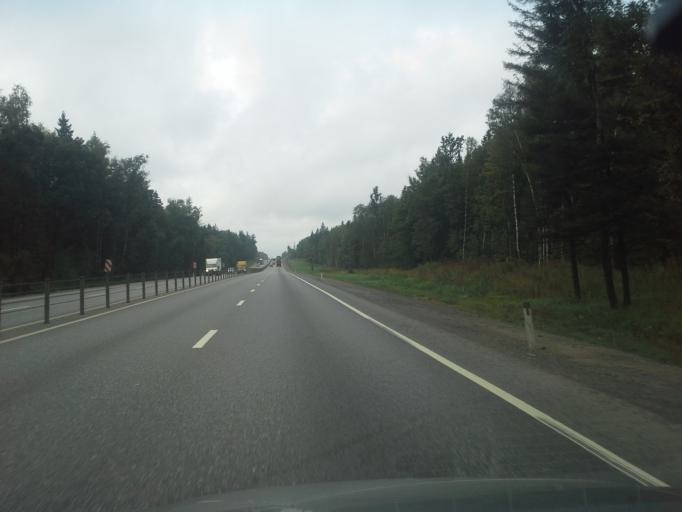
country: RU
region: Moskovskaya
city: Kubinka
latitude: 55.5805
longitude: 36.7884
